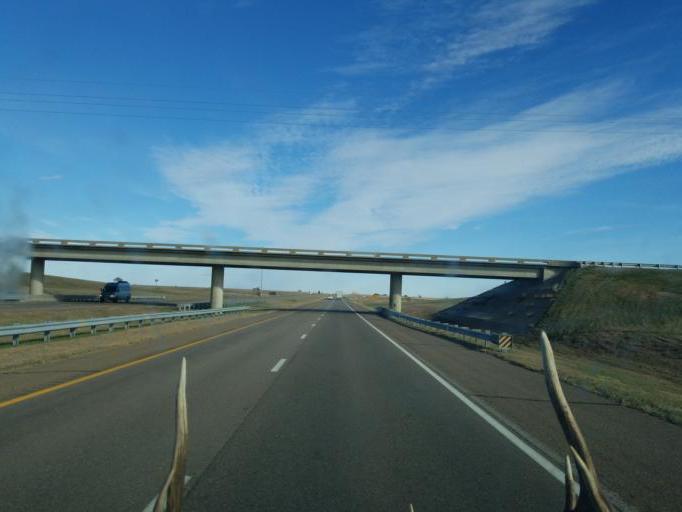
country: US
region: Kansas
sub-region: Ellis County
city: Hays
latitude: 38.8782
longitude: -99.2445
